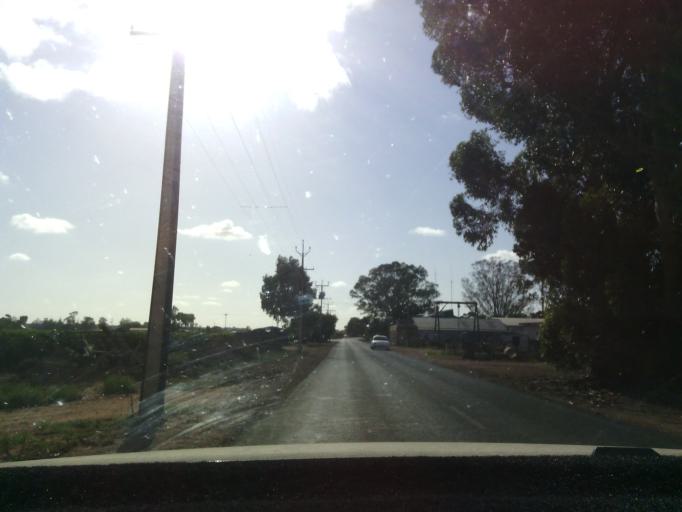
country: AU
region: South Australia
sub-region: Berri and Barmera
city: Monash
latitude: -34.2466
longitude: 140.5537
